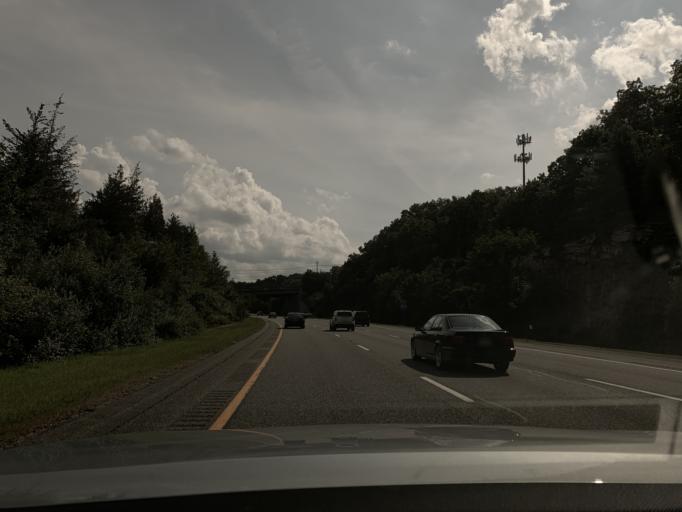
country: US
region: Rhode Island
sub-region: Providence County
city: Smithfield
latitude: 41.8985
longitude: -71.5231
